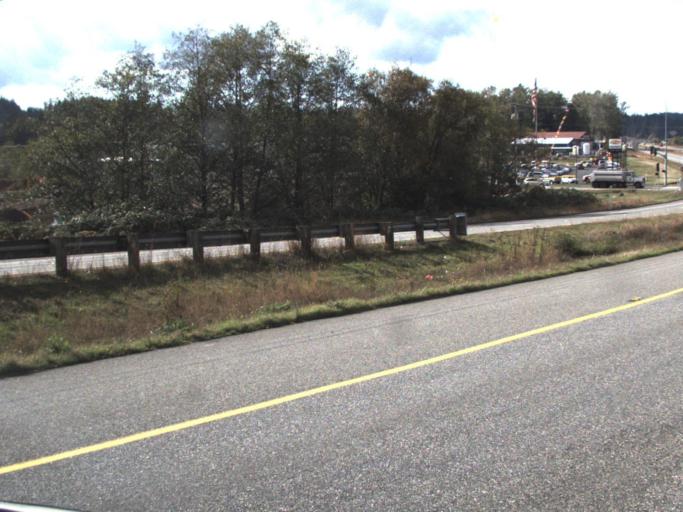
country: US
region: Washington
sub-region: Skagit County
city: Anacortes
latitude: 48.4632
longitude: -122.5419
